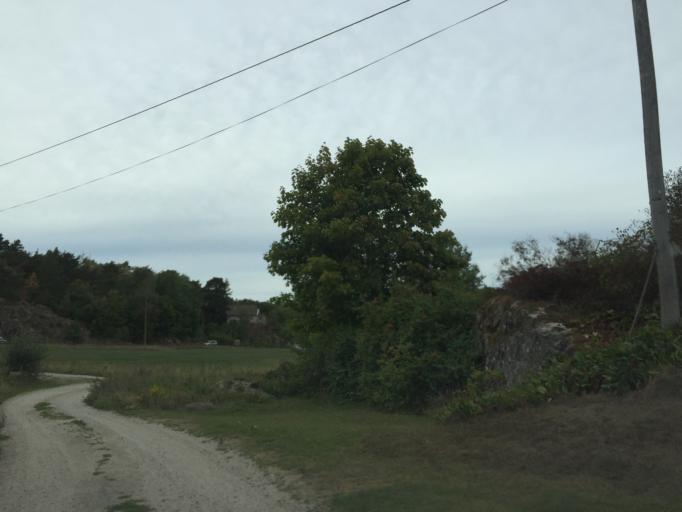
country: NO
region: Ostfold
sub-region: Hvaler
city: Skjaerhalden
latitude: 59.0355
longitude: 11.0542
